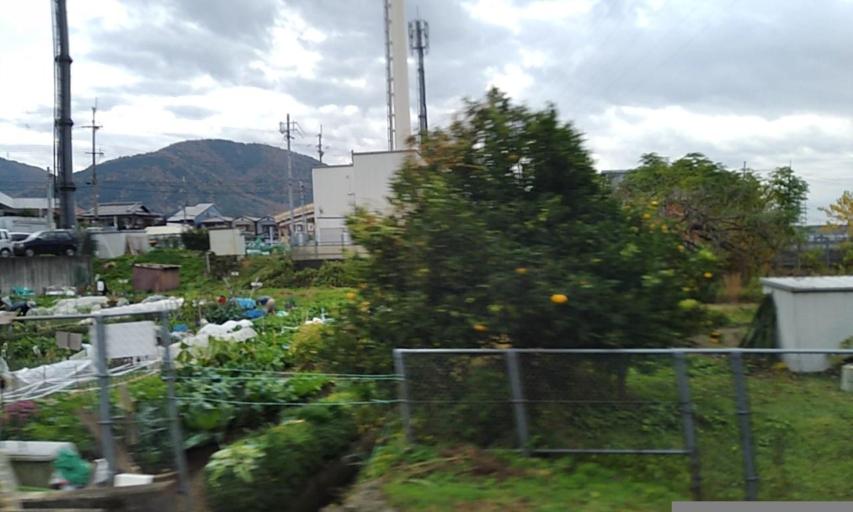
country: JP
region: Shiga Prefecture
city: Otsu-shi
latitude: 34.9923
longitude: 135.8309
